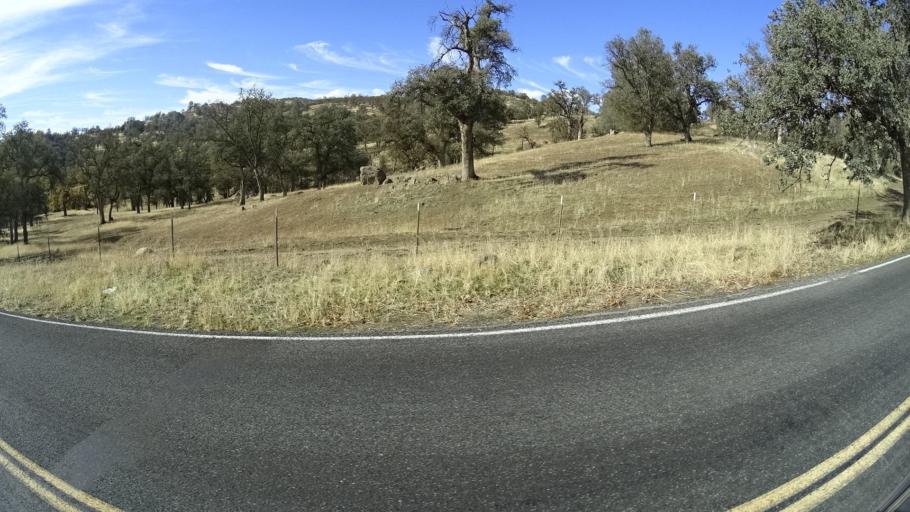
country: US
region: California
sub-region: Kern County
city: Alta Sierra
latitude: 35.6953
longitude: -118.7300
